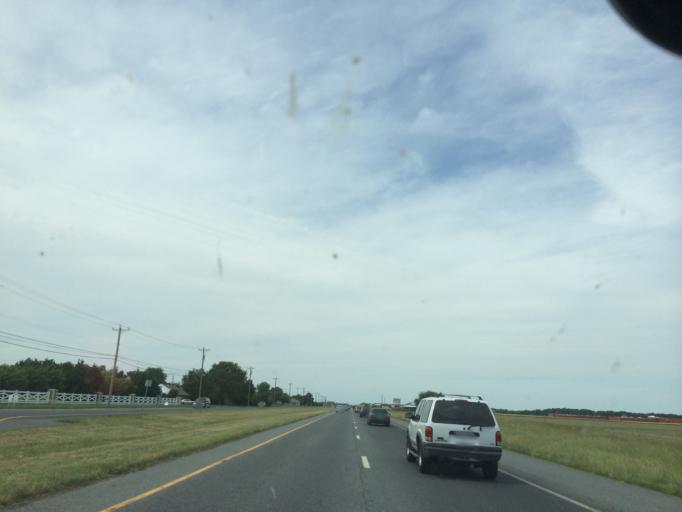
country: US
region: Delaware
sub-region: Sussex County
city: Bridgeville
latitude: 38.7119
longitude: -75.5887
